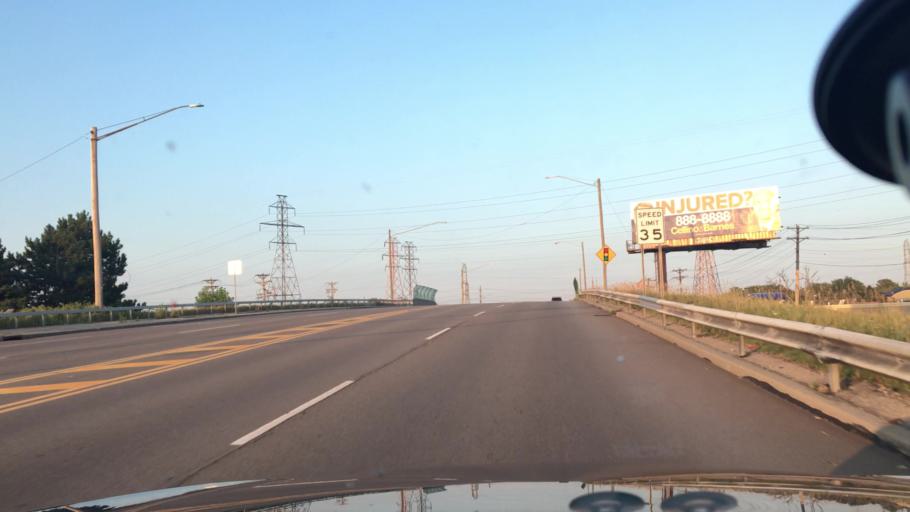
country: US
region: New York
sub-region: Erie County
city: West Seneca
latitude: 42.8285
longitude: -78.7869
